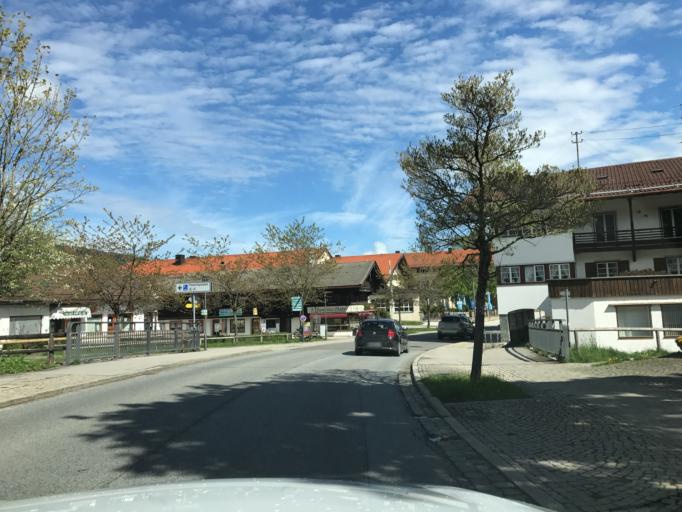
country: DE
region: Bavaria
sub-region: Upper Bavaria
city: Bad Wiessee
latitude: 47.7111
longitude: 11.7254
